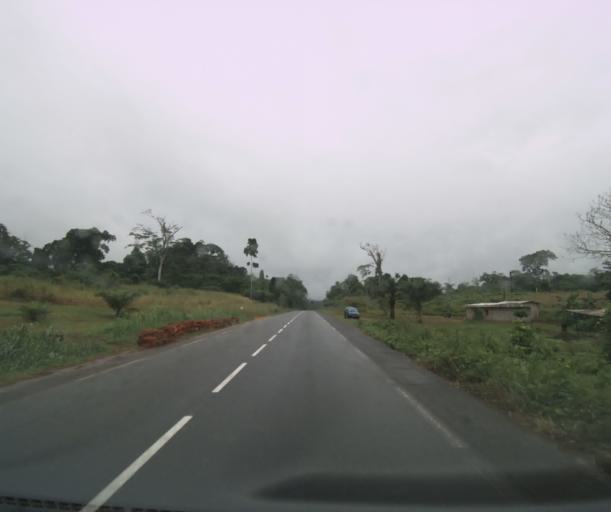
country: CM
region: Littoral
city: Dizangue
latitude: 3.3562
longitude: 10.1011
